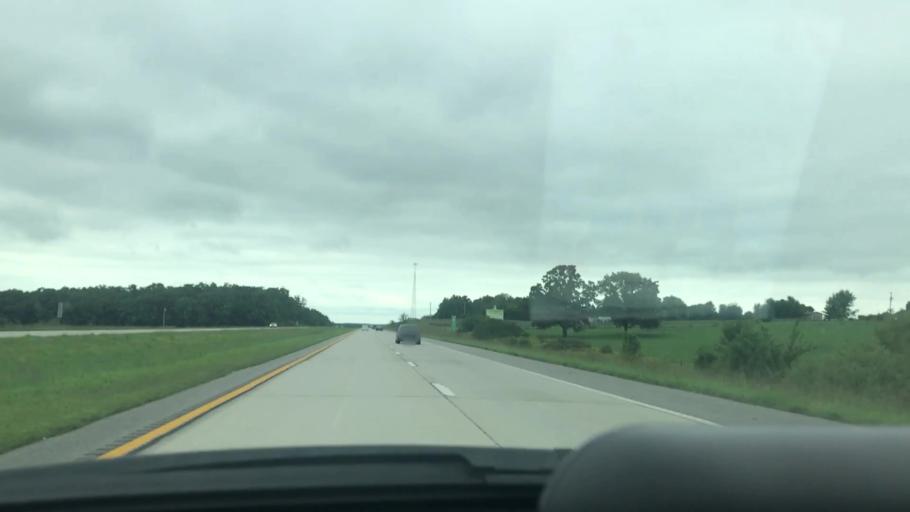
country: US
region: Missouri
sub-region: Greene County
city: Fair Grove
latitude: 37.4997
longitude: -93.1389
